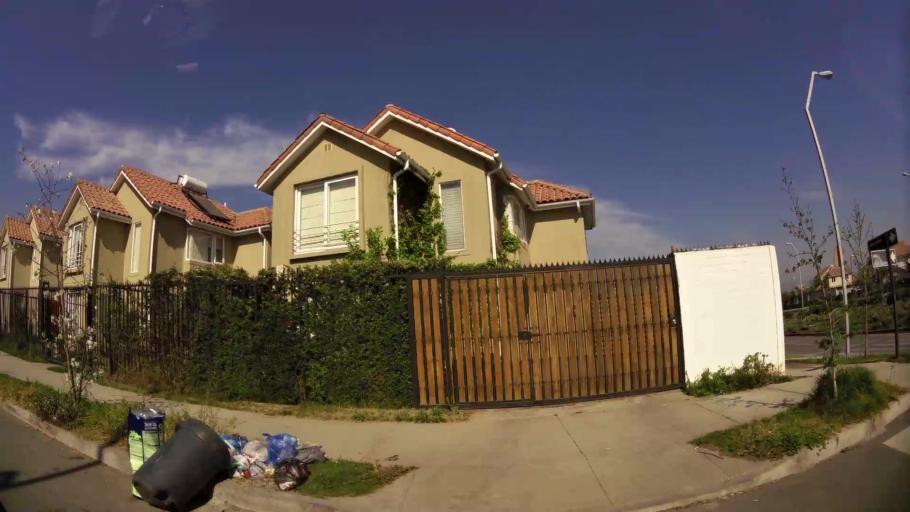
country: CL
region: Santiago Metropolitan
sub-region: Provincia de Talagante
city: Penaflor
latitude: -33.5717
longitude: -70.8236
